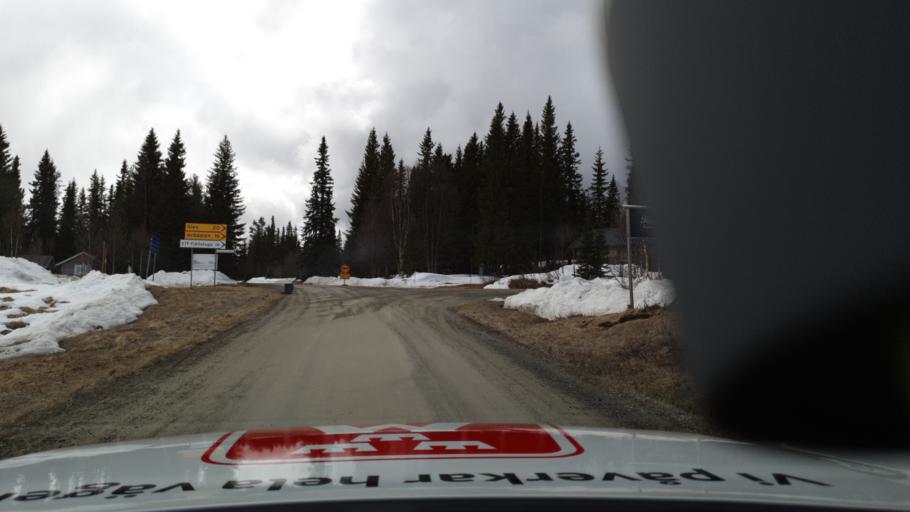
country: SE
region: Jaemtland
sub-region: Are Kommun
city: Jarpen
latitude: 62.8375
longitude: 13.8187
